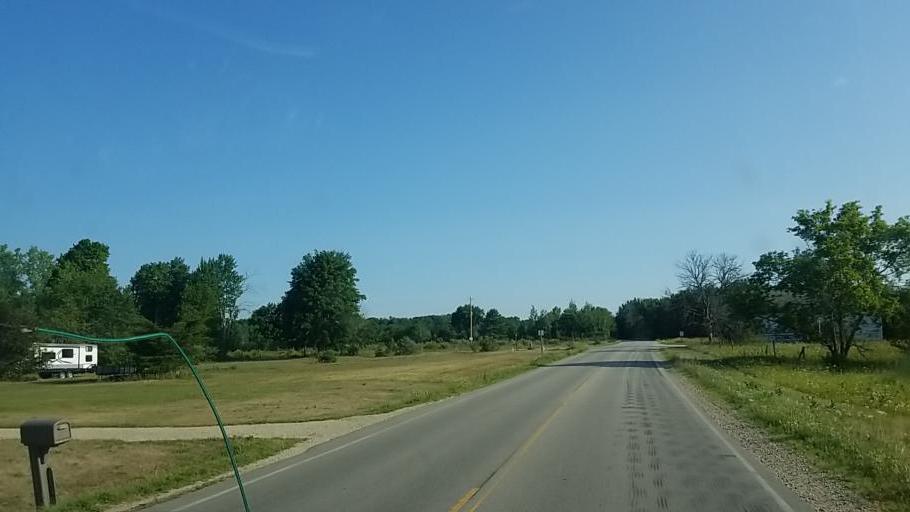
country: US
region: Michigan
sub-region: Newaygo County
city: Fremont
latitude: 43.3792
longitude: -85.9393
